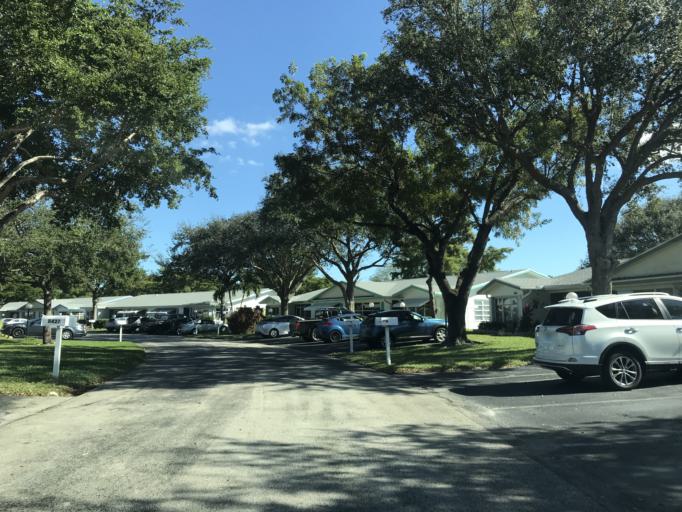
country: US
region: Florida
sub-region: Broward County
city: Plantation
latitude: 26.1361
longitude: -80.2616
